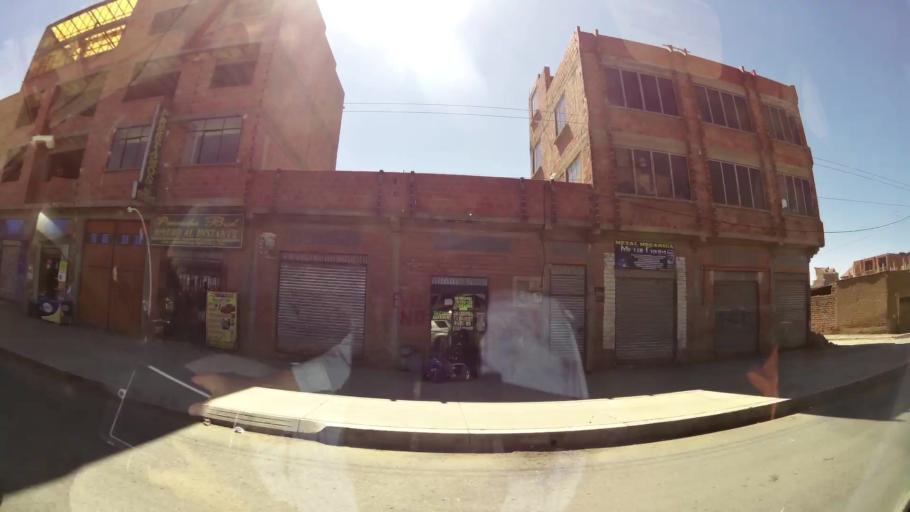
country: BO
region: La Paz
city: La Paz
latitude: -16.5362
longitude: -68.2051
